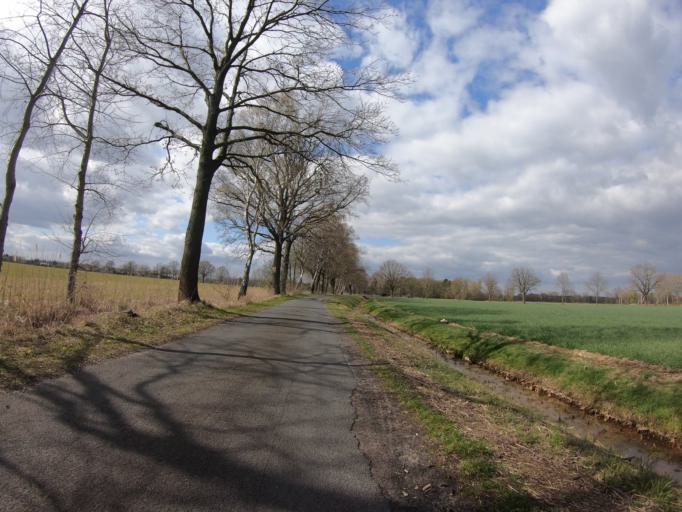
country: DE
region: Lower Saxony
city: Gifhorn
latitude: 52.4776
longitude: 10.5889
